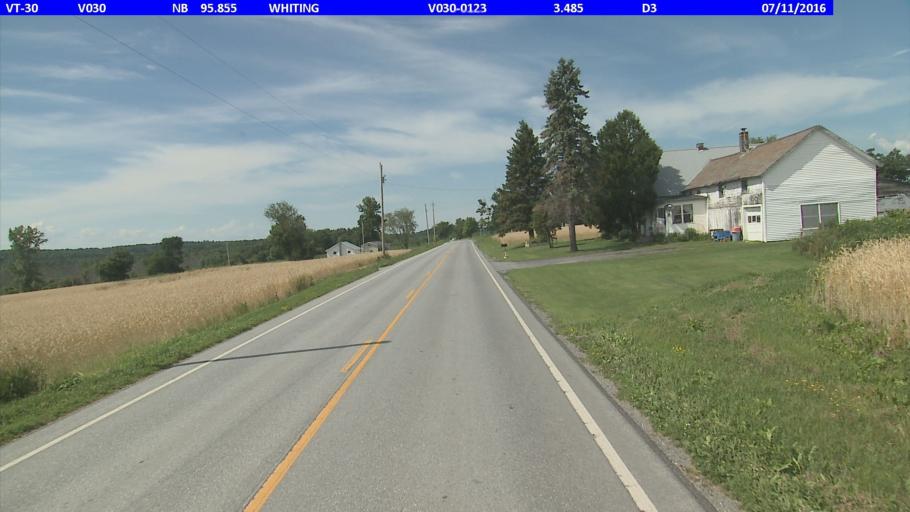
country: US
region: Vermont
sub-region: Addison County
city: Middlebury (village)
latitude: 43.8876
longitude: -73.2015
